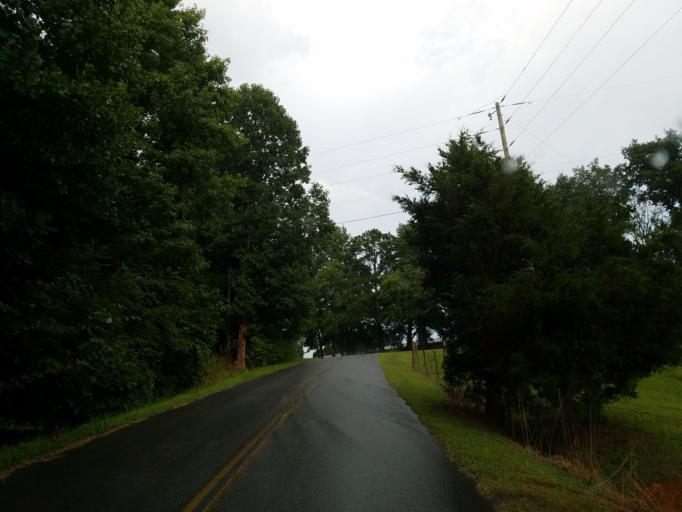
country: US
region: Georgia
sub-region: Bartow County
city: Rydal
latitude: 34.3885
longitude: -84.6541
